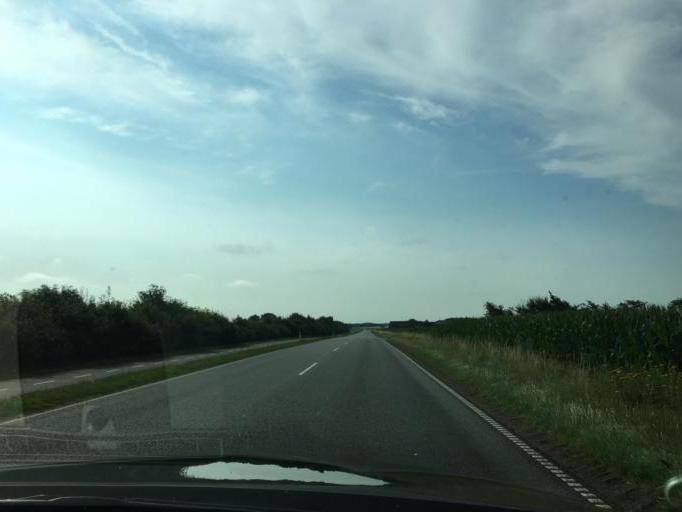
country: DK
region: South Denmark
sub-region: Varde Kommune
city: Oksbol
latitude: 55.7434
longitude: 8.3302
